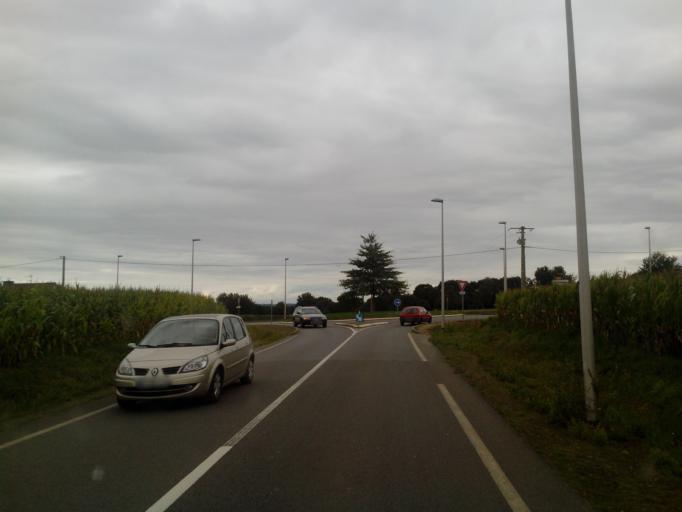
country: FR
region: Brittany
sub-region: Departement d'Ille-et-Vilaine
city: Betton
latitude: 48.1797
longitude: -1.6286
